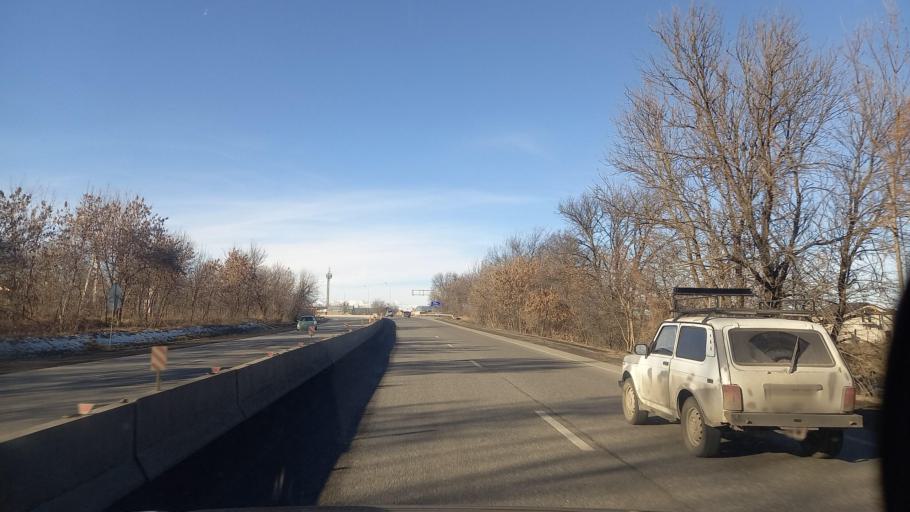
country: RU
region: North Ossetia
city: Gizel'
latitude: 43.0290
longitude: 44.5829
